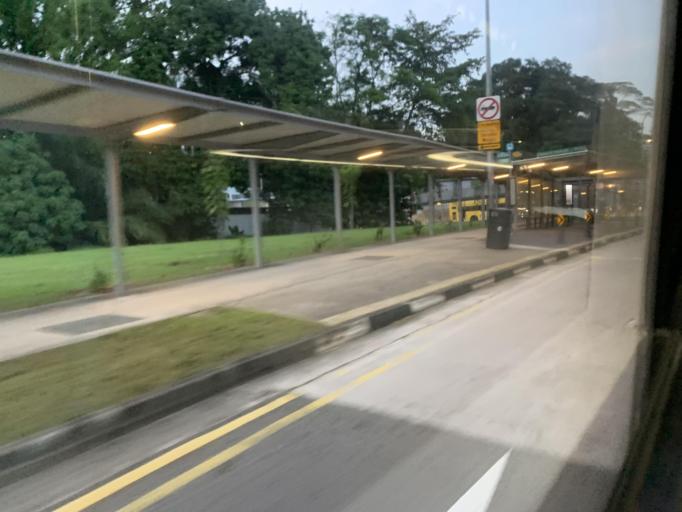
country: MY
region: Johor
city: Johor Bahru
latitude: 1.3613
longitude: 103.7669
